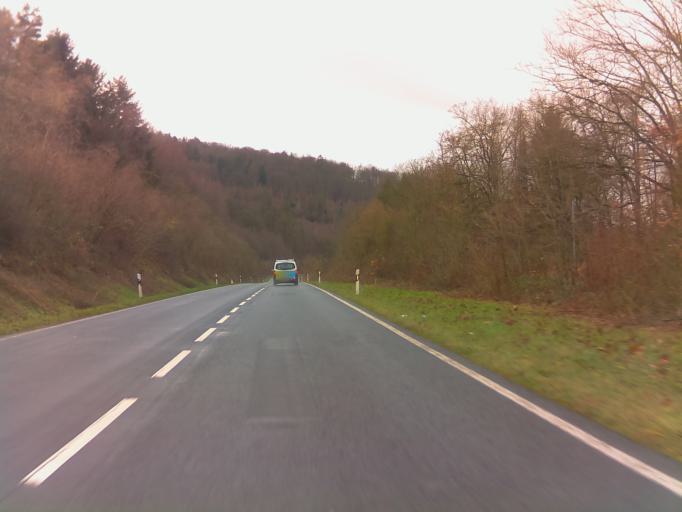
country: DE
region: Hesse
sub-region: Regierungsbezirk Darmstadt
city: Steinau an der Strasse
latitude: 50.3081
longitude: 9.4375
